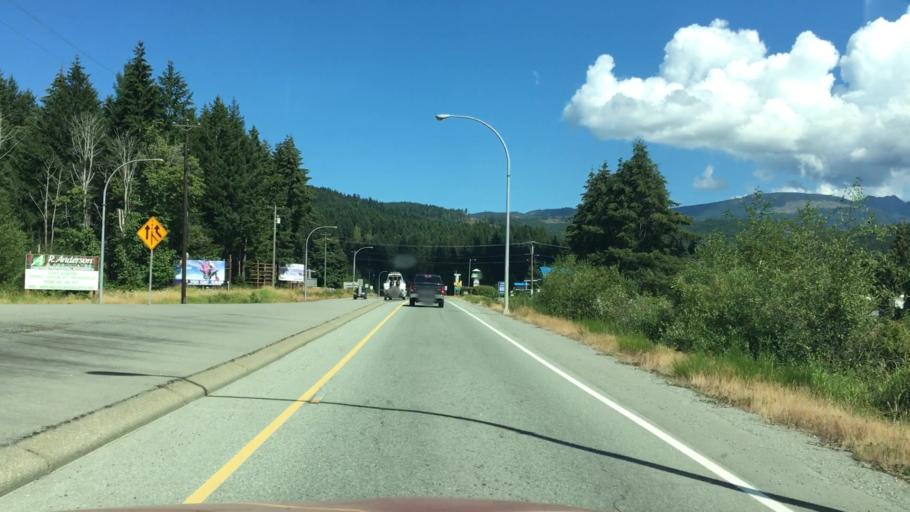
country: CA
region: British Columbia
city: Port Alberni
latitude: 49.2641
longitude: -124.7578
